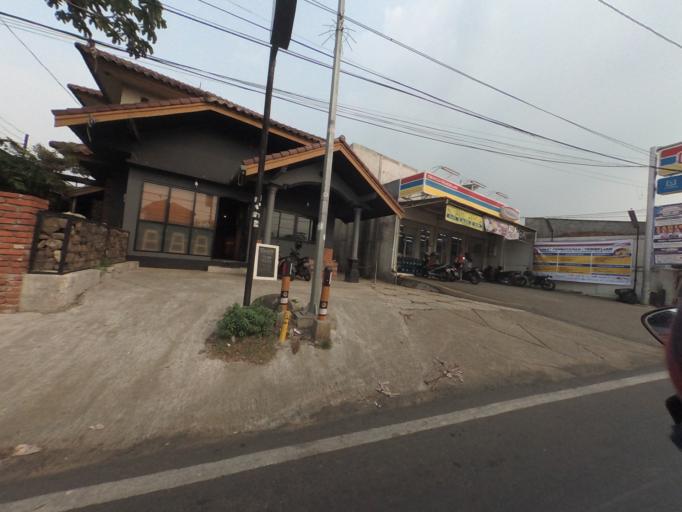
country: ID
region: West Java
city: Ciampea
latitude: -6.5736
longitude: 106.6662
